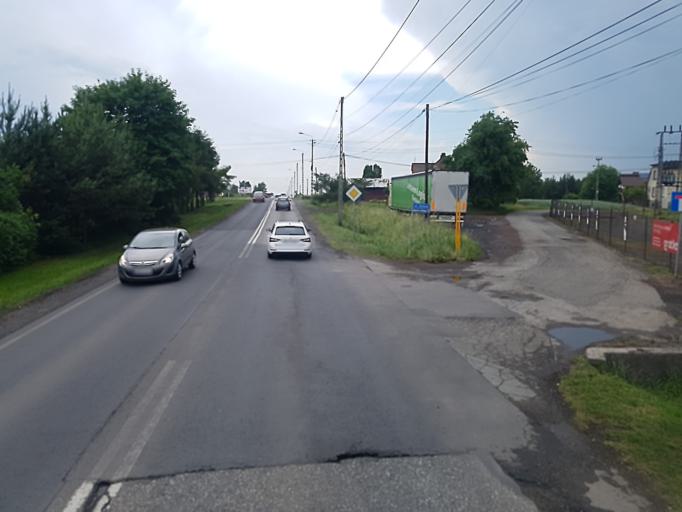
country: PL
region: Silesian Voivodeship
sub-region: Powiat wodzislawski
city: Mszana
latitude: 49.9835
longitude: 18.5111
